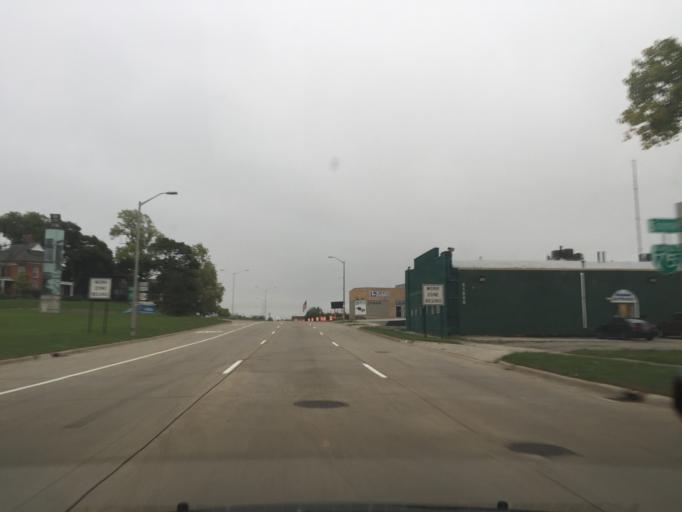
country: US
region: Michigan
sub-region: Oakland County
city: Pontiac
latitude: 42.6304
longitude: -83.2897
